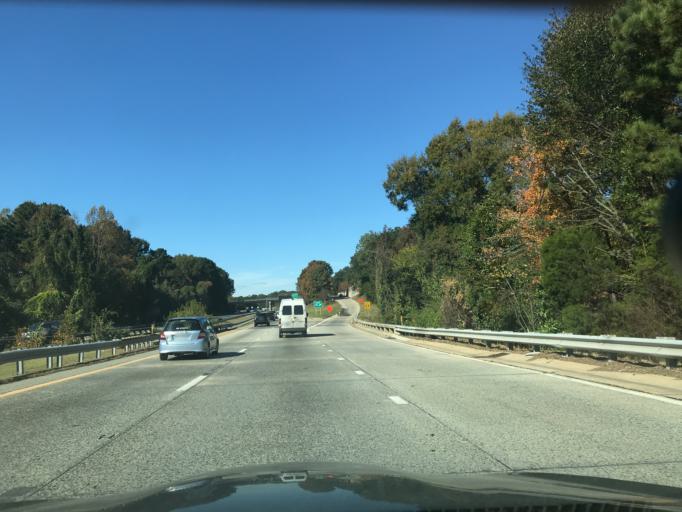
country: US
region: North Carolina
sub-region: Durham County
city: Durham
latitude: 36.0019
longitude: -78.9171
